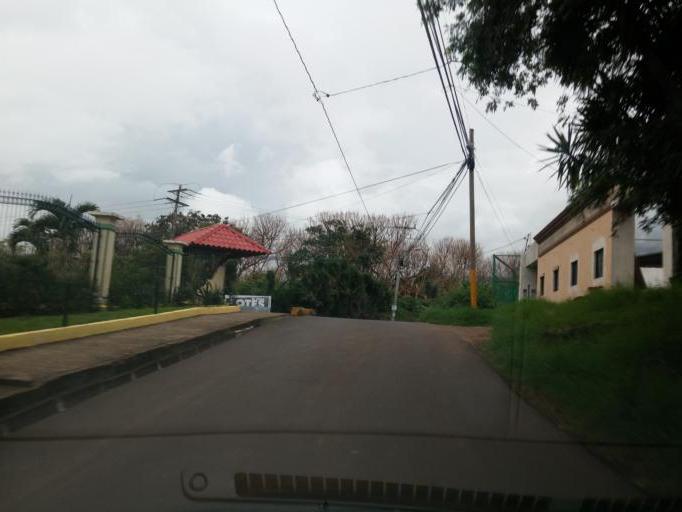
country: CR
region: Heredia
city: Mercedes
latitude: 10.0359
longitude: -84.1318
